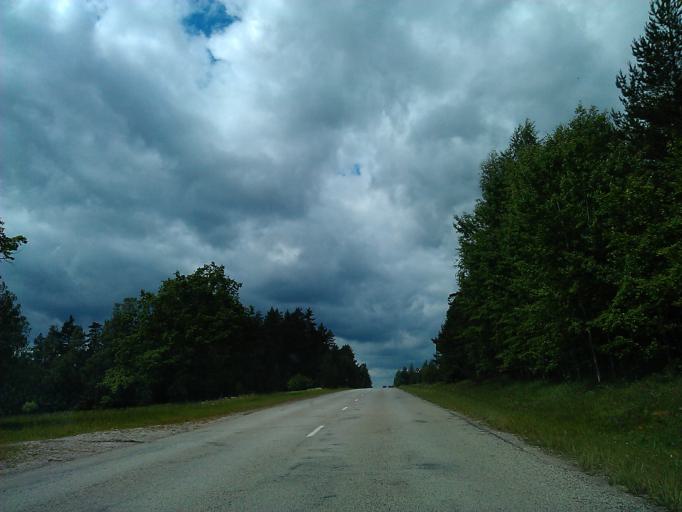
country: LV
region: Talsu Rajons
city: Stende
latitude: 57.0845
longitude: 22.4778
